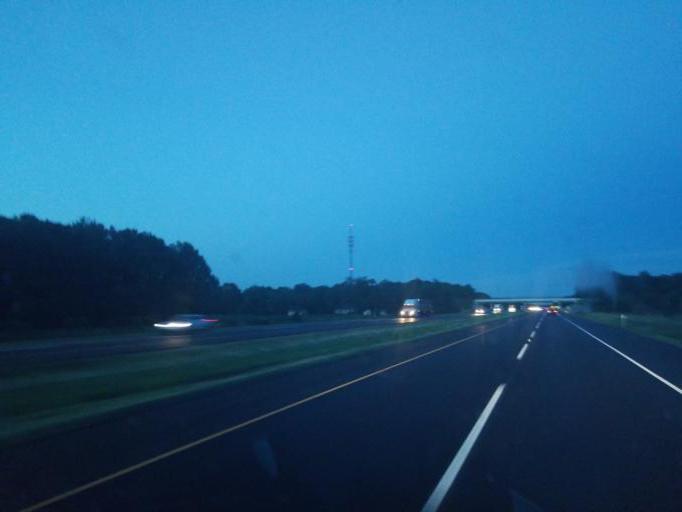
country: US
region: Indiana
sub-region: Saint Joseph County
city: Granger
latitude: 41.7311
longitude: -86.0854
